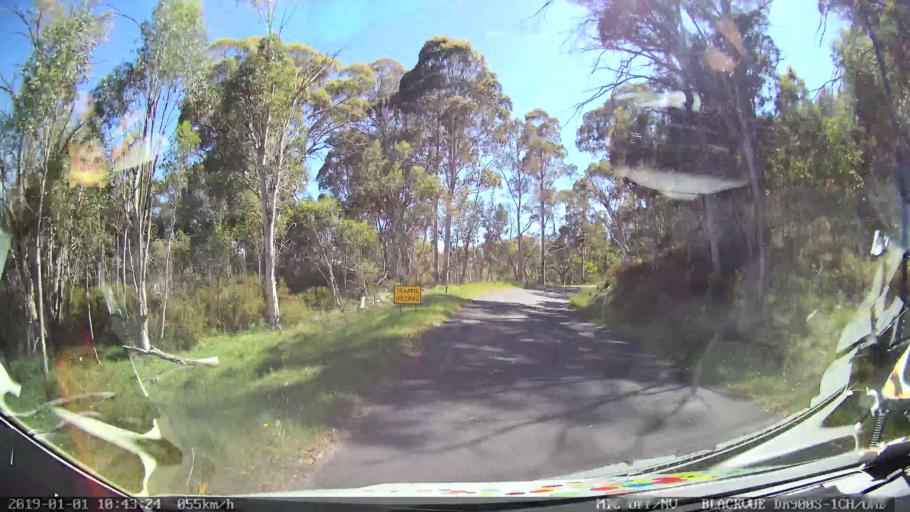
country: AU
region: New South Wales
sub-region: Snowy River
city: Jindabyne
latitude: -36.0363
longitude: 148.3244
